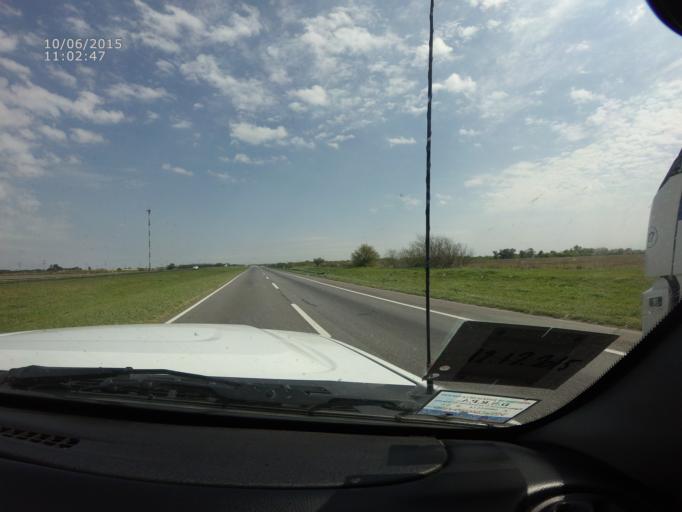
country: AR
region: Santa Fe
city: Villa Constitucion
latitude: -33.2440
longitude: -60.4367
